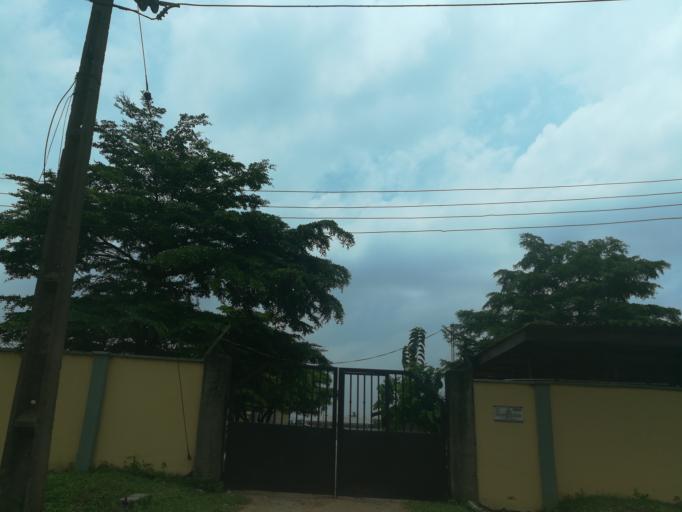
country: NG
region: Lagos
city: Ikorodu
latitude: 6.6227
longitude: 3.5221
